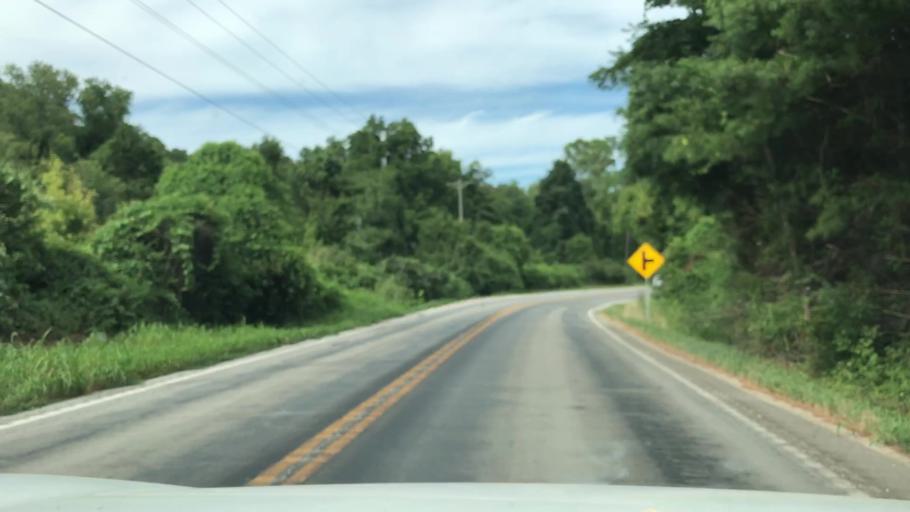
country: US
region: Missouri
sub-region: Saint Charles County
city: Weldon Spring
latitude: 38.6556
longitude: -90.7707
